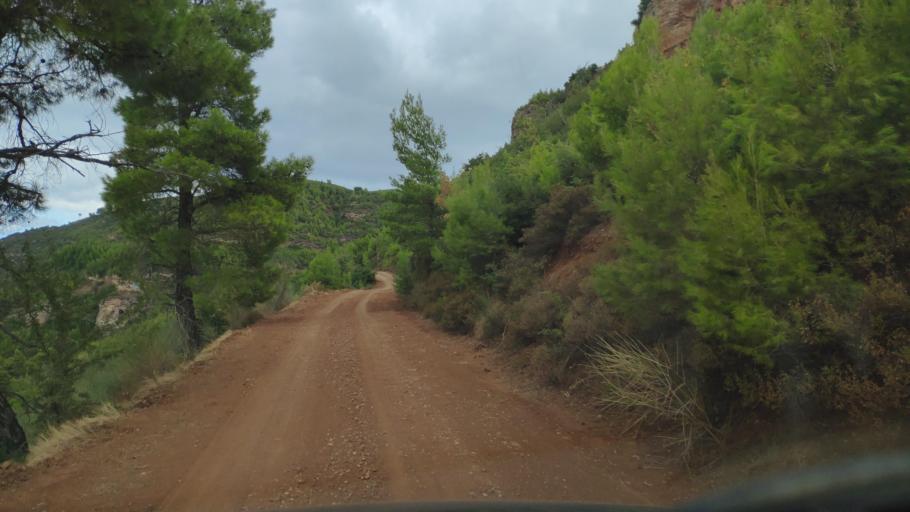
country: GR
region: West Greece
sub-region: Nomos Achaias
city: Temeni
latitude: 38.1656
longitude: 22.1507
